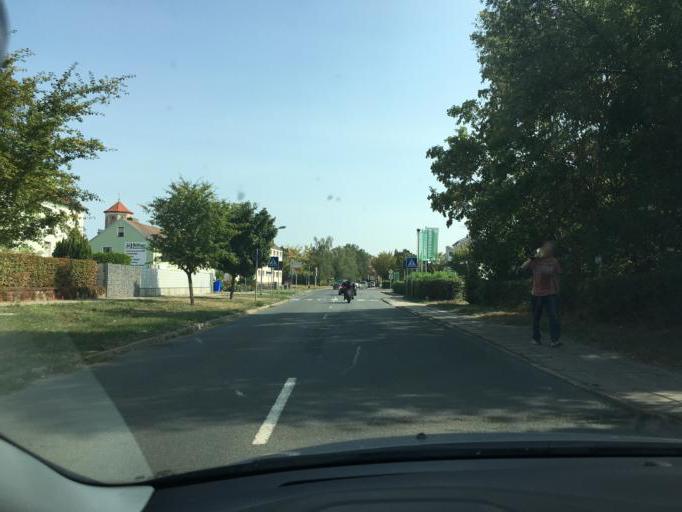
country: DE
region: Saxony-Anhalt
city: Barby
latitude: 51.9737
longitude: 11.8824
